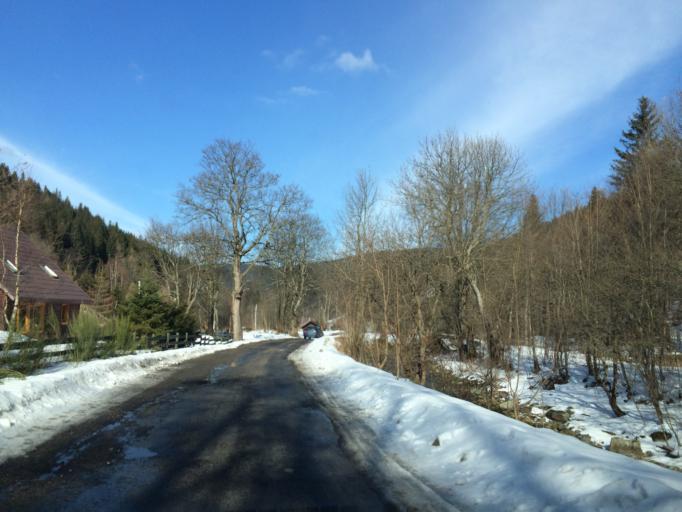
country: CZ
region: Olomoucky
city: Vapenna
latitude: 50.2654
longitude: 17.0011
